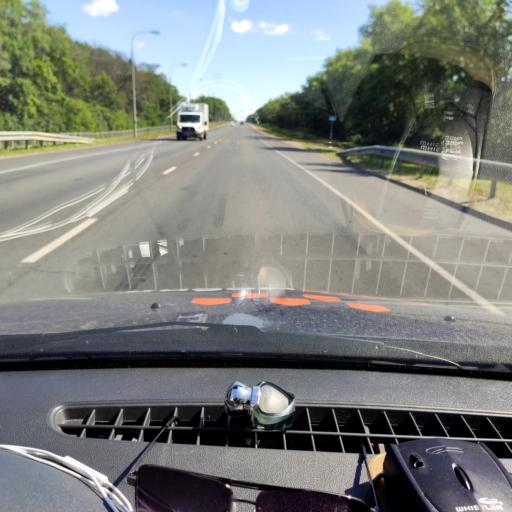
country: RU
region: Lipetsk
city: Khlevnoye
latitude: 52.1980
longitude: 39.1203
